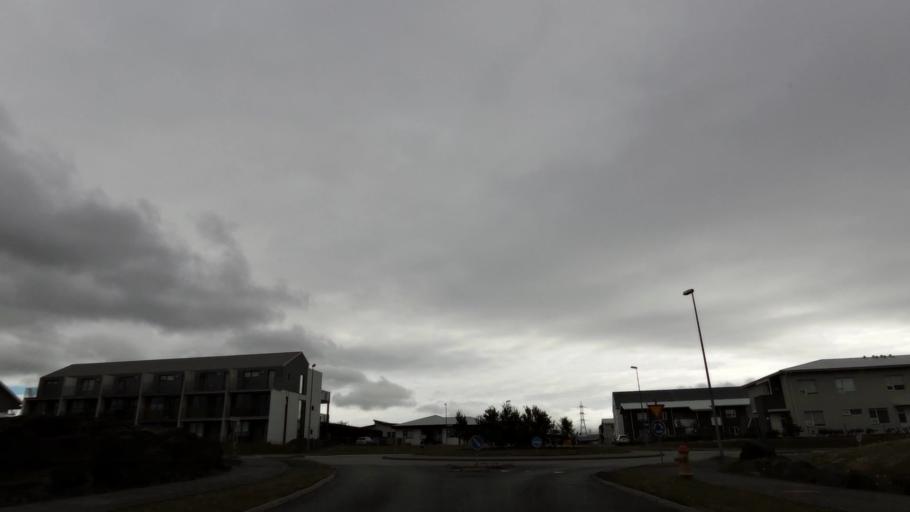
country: IS
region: Capital Region
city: Hafnarfjoerdur
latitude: 64.0450
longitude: -21.9788
